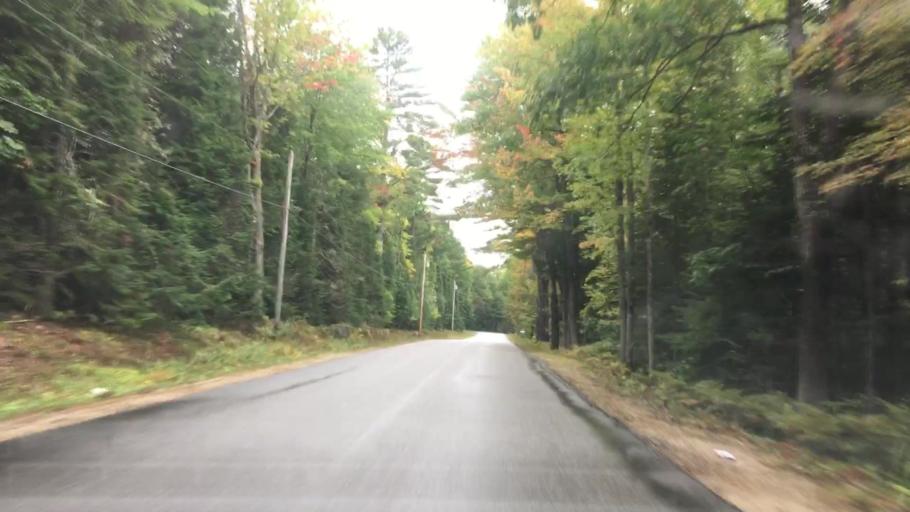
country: US
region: Maine
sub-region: Cumberland County
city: Harrison
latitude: 44.0377
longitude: -70.6061
